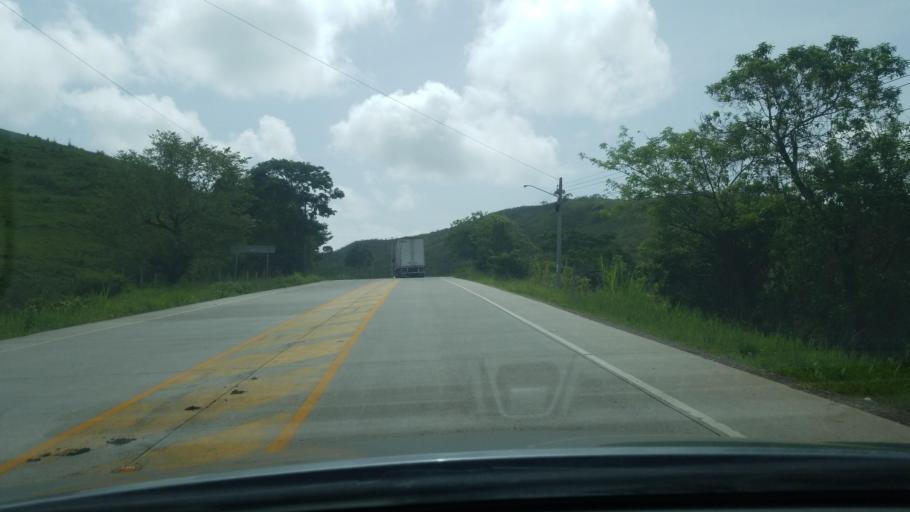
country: HN
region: Copan
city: San Jeronimo
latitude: 14.9349
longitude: -88.9228
